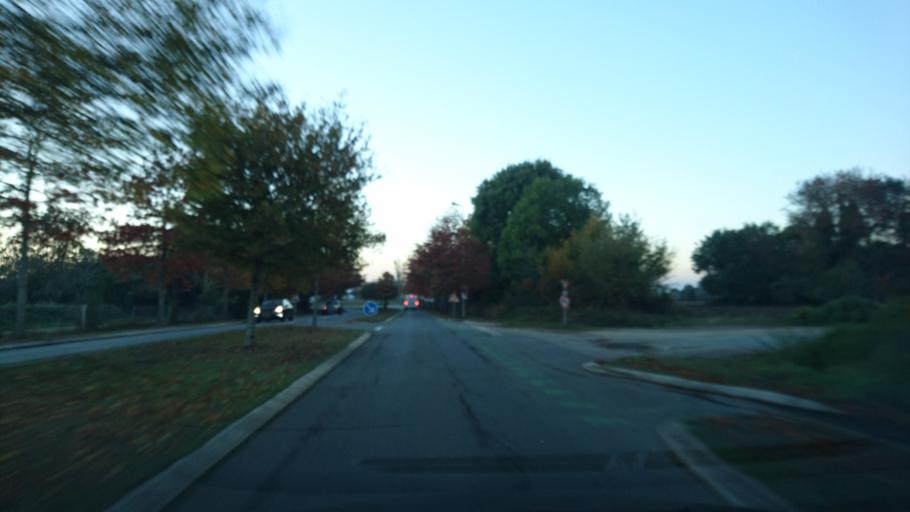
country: FR
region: Brittany
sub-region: Departement du Morbihan
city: Auray
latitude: 47.6820
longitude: -3.0165
